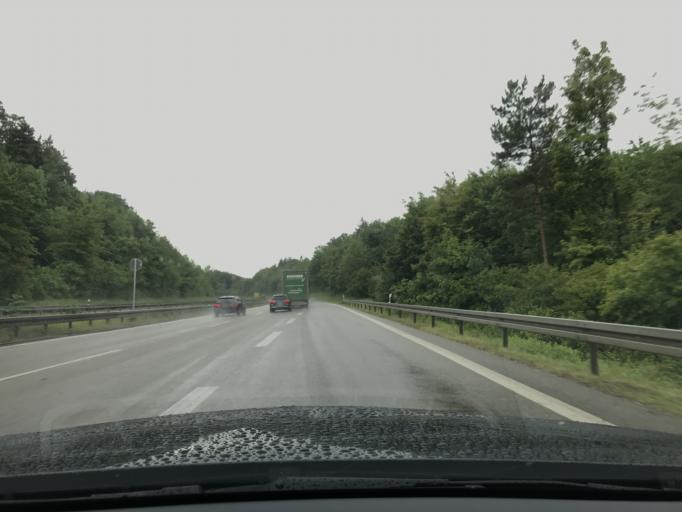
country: DE
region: Baden-Wuerttemberg
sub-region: Regierungsbezirk Stuttgart
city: Winnenden
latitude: 48.8712
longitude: 9.3791
